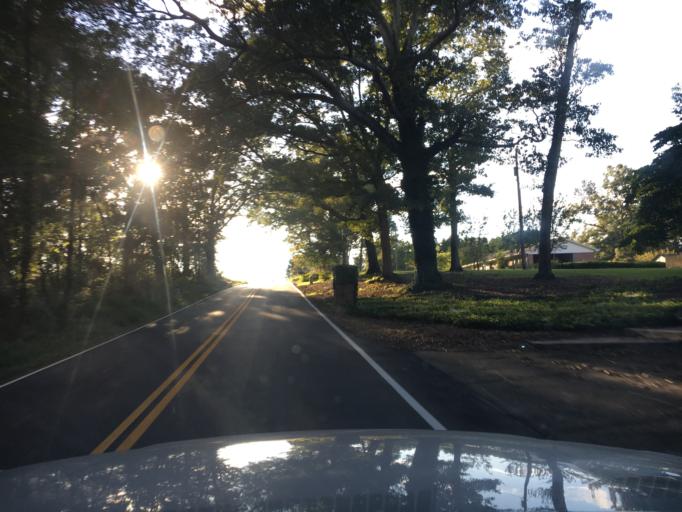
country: US
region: South Carolina
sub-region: Spartanburg County
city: Roebuck
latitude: 34.9011
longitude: -82.0010
